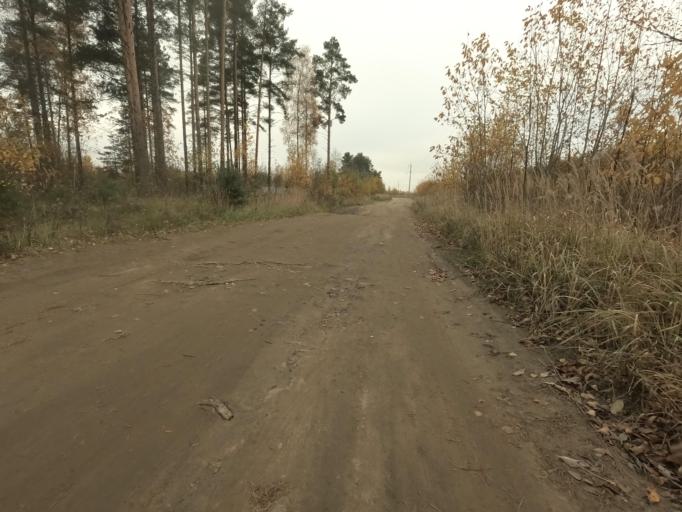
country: RU
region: Leningrad
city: Kirovsk
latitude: 59.8528
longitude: 30.9845
